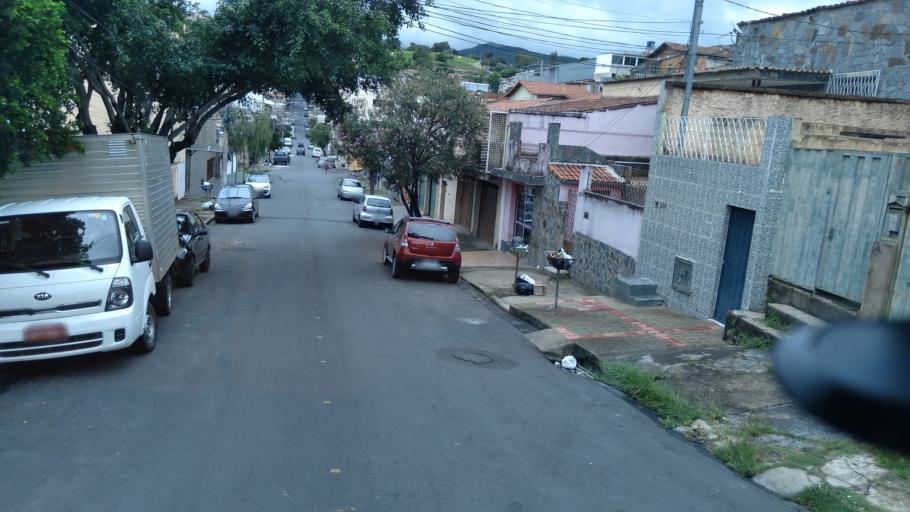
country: BR
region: Minas Gerais
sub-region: Belo Horizonte
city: Belo Horizonte
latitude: -19.9128
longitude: -43.8965
